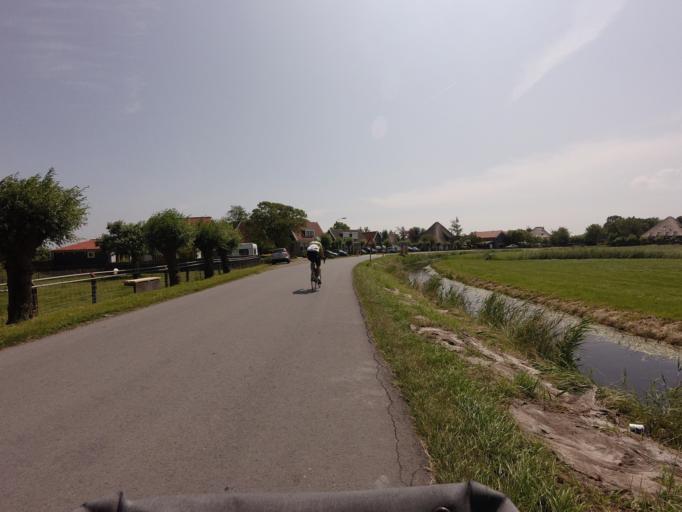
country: NL
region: North Holland
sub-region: Gemeente Opmeer
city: Opmeer
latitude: 52.6591
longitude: 4.9501
